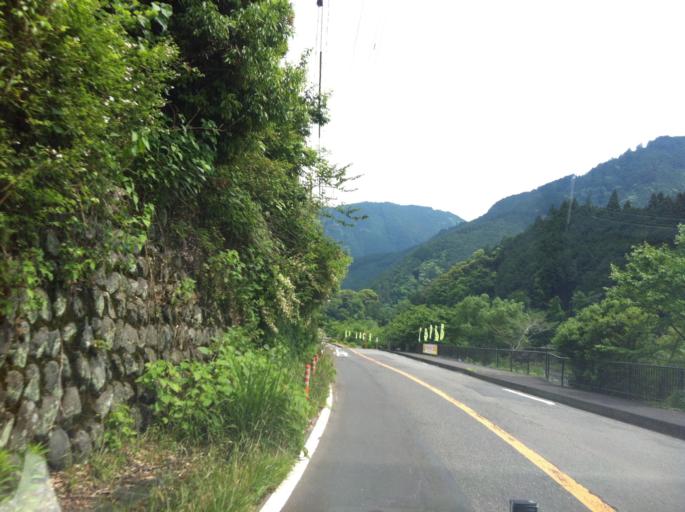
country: JP
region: Shizuoka
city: Shizuoka-shi
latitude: 35.1109
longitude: 138.3302
